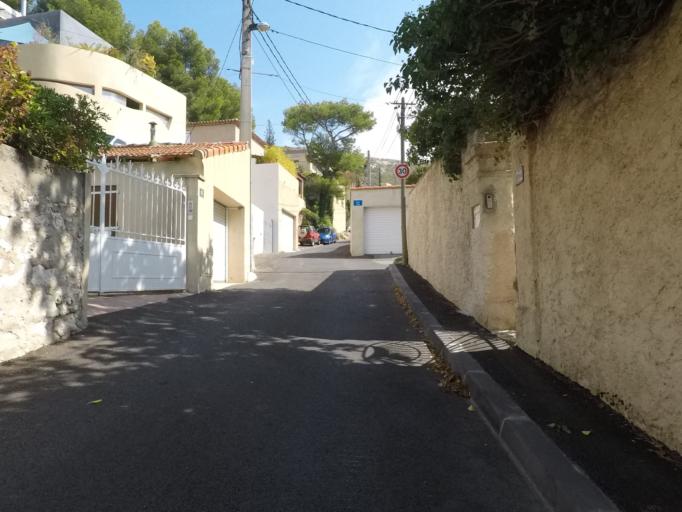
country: FR
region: Provence-Alpes-Cote d'Azur
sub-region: Departement des Bouches-du-Rhone
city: Marseille 09
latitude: 43.2533
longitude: 5.4309
